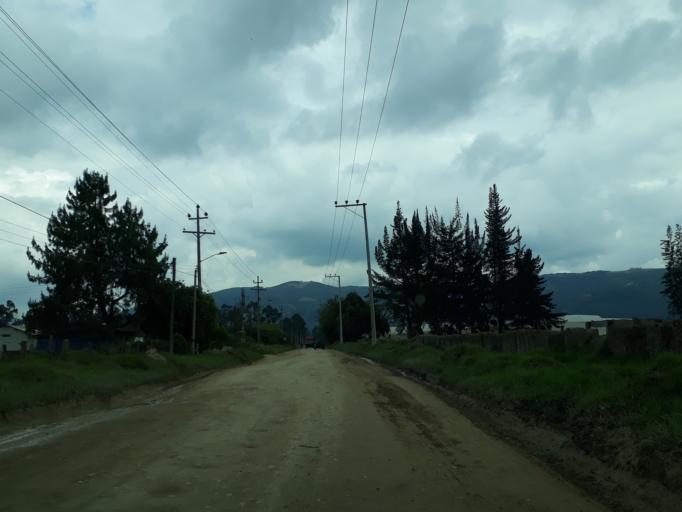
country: CO
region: Cundinamarca
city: Sesquile
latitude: 5.0658
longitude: -73.8092
